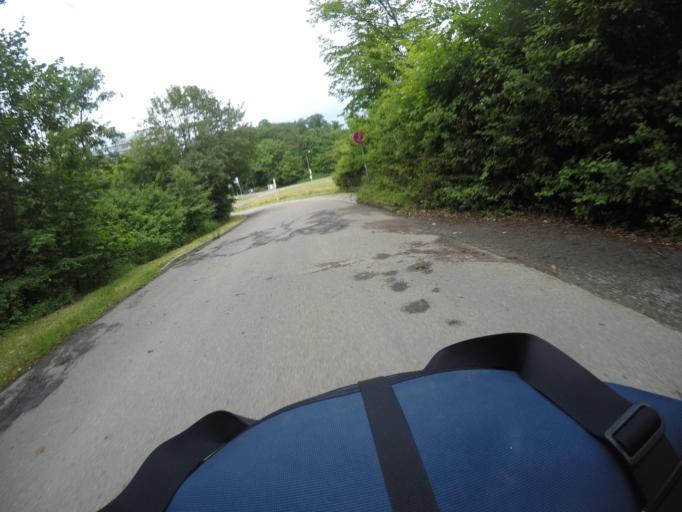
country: DE
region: Baden-Wuerttemberg
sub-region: Regierungsbezirk Stuttgart
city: Gerlingen
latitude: 48.7863
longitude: 9.0665
